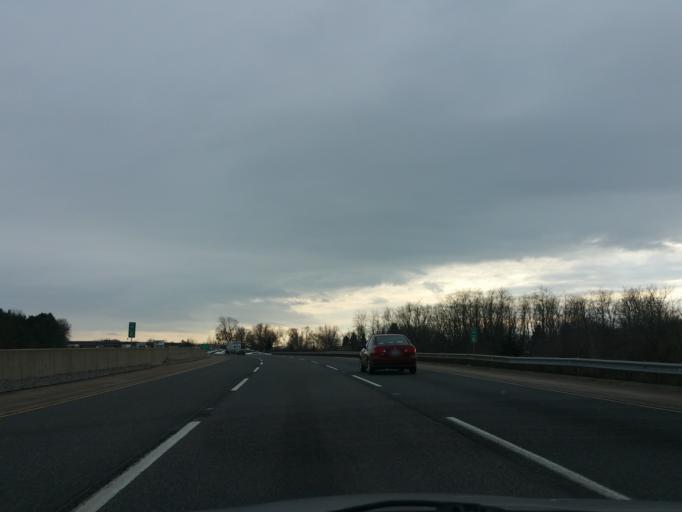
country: US
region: Illinois
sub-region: Winnebago County
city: Roscoe
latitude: 42.4104
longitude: -88.9855
